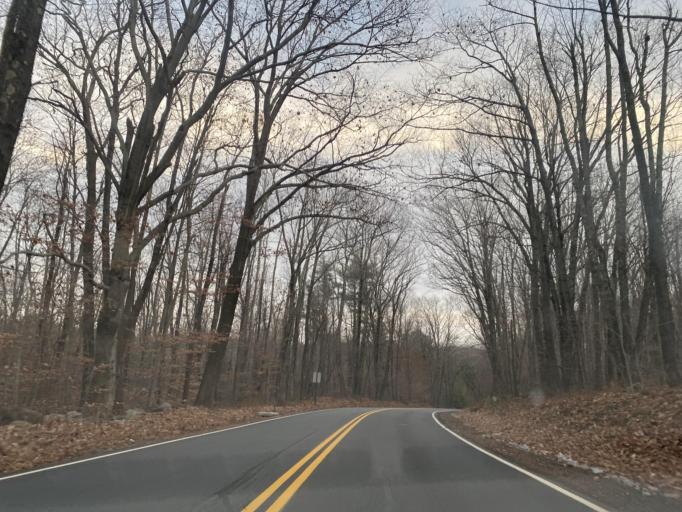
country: US
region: Massachusetts
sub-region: Worcester County
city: Leicester
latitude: 42.2778
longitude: -71.9097
